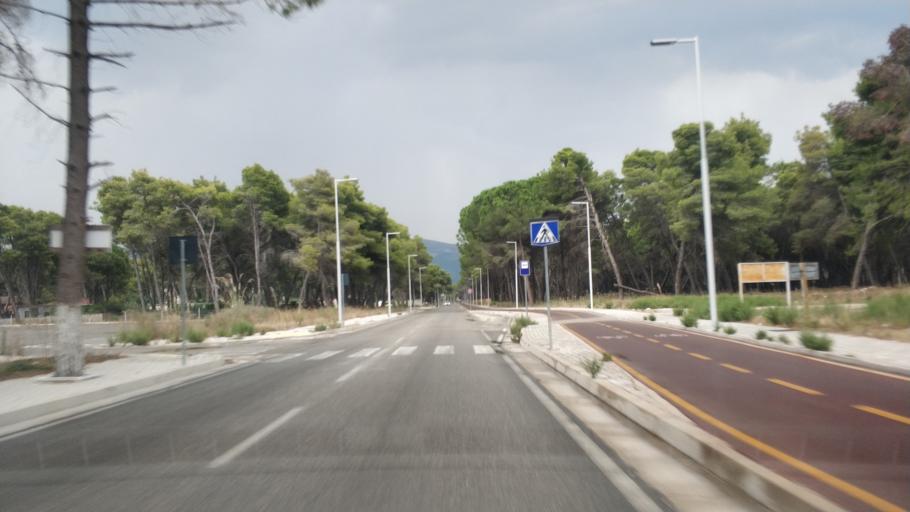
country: AL
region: Vlore
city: Vlore
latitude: 40.4651
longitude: 19.4626
